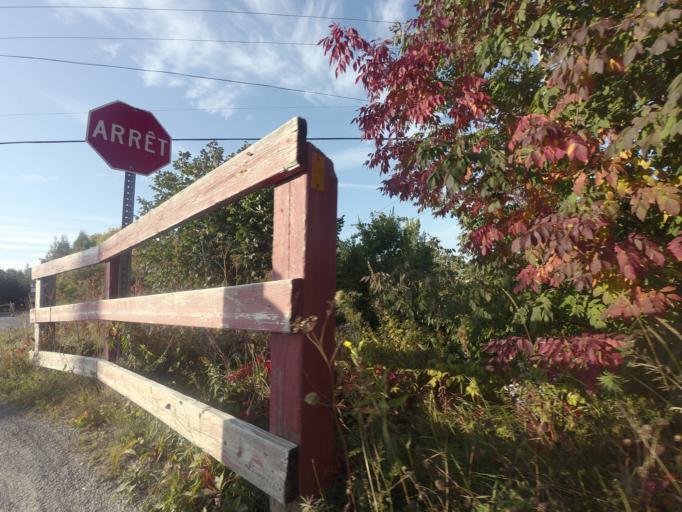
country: CA
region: Quebec
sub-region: Laurentides
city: Saint-Jerome
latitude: 45.8089
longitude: -74.0189
